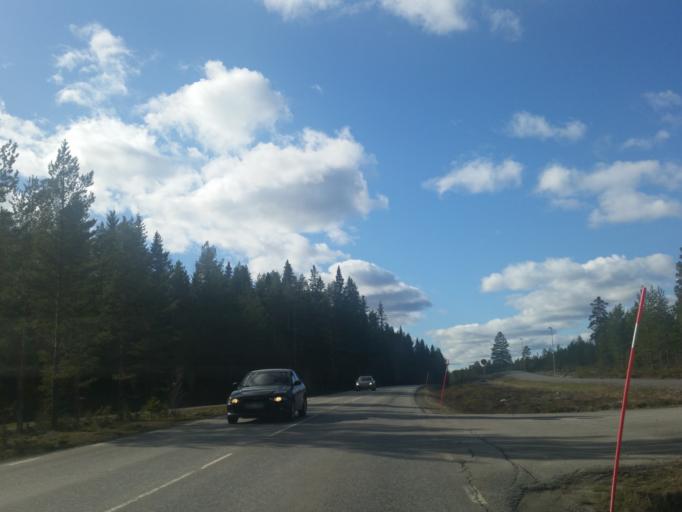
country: SE
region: Vaesterbotten
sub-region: Robertsfors Kommun
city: Robertsfors
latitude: 64.1771
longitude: 20.9033
